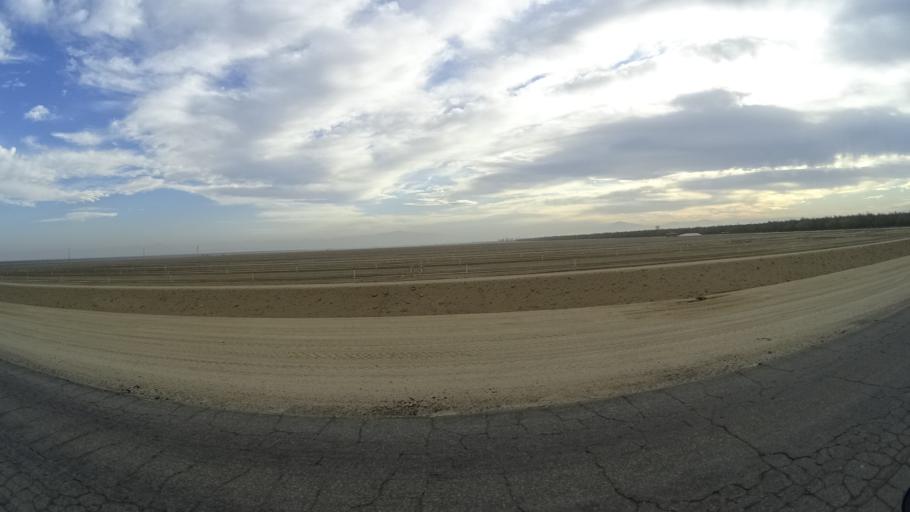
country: US
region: California
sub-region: Kern County
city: Rosedale
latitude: 35.4139
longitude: -119.1988
